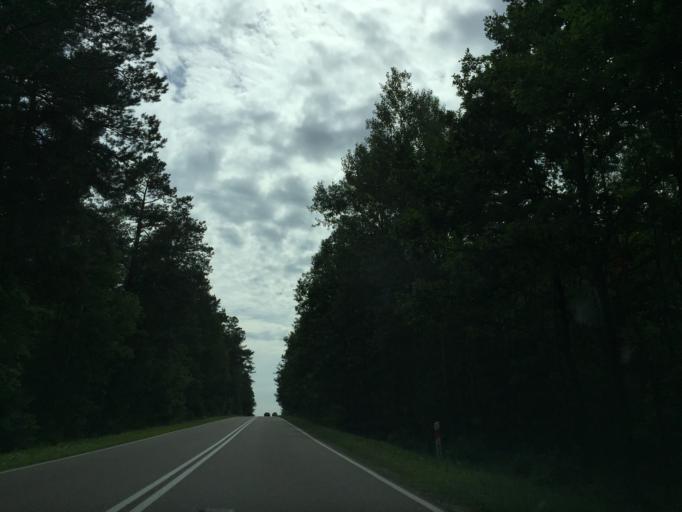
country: PL
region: Podlasie
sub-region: Powiat siemiatycki
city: Dziadkowice
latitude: 52.5092
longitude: 22.8969
